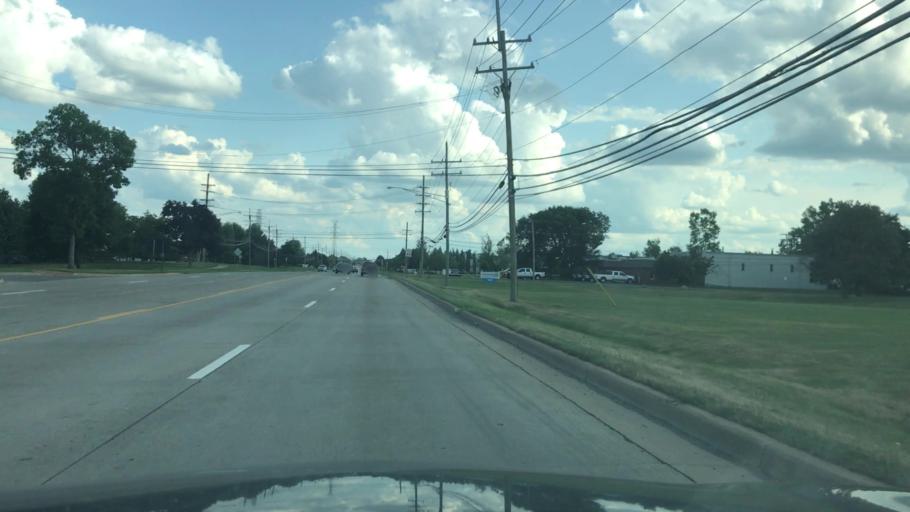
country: US
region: Michigan
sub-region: Oakland County
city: Wixom
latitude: 42.5203
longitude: -83.5377
